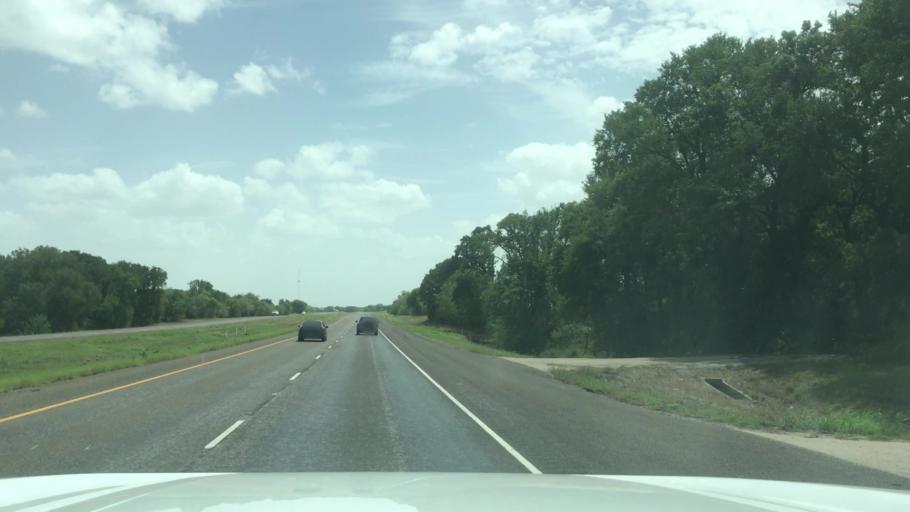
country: US
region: Texas
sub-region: Falls County
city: Marlin
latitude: 31.2909
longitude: -96.8752
